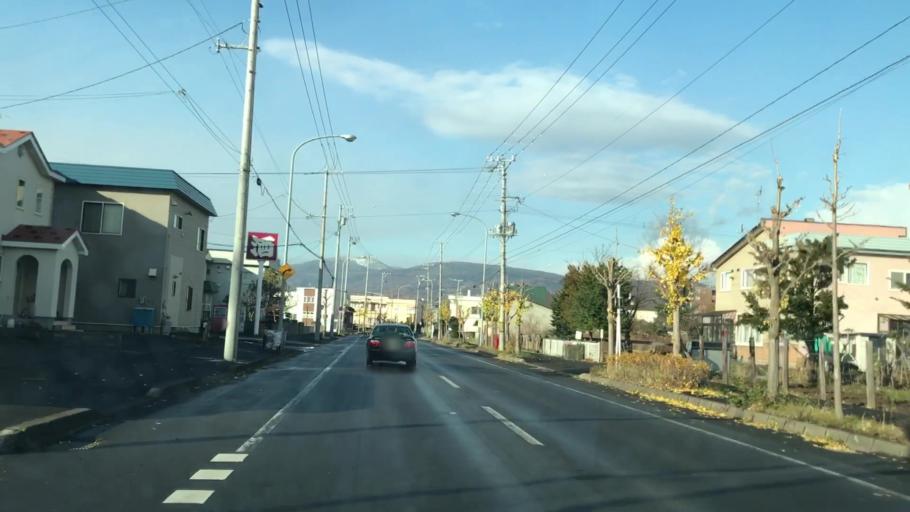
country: JP
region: Hokkaido
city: Yoichi
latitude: 43.1829
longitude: 140.8011
